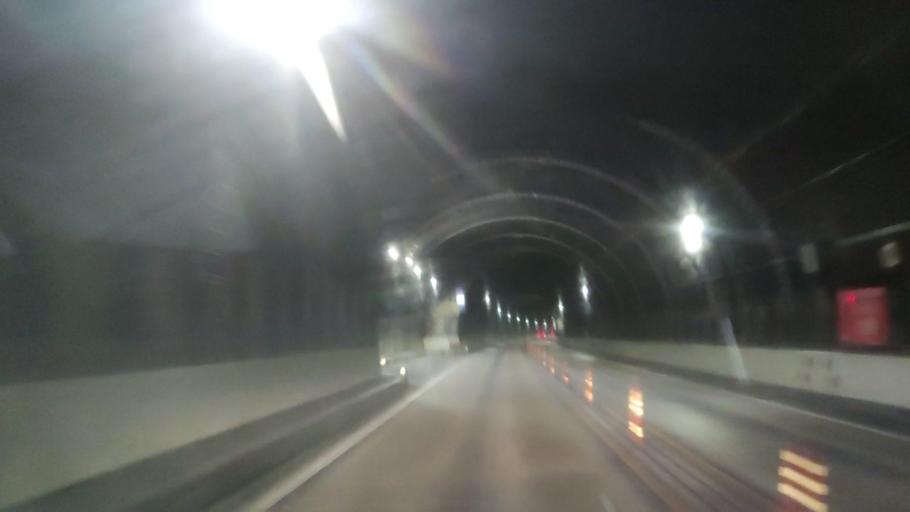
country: JP
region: Hiroshima
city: Innoshima
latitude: 34.1812
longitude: 133.0685
